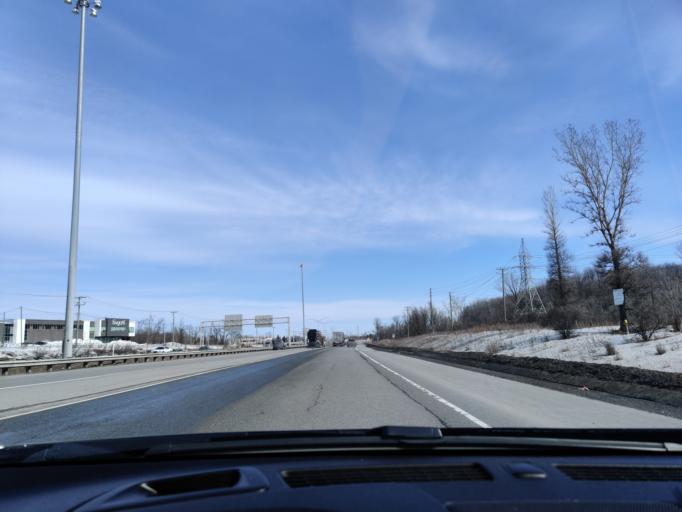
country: CA
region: Quebec
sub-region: Laurentides
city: Boisbriand
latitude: 45.6033
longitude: -73.8594
